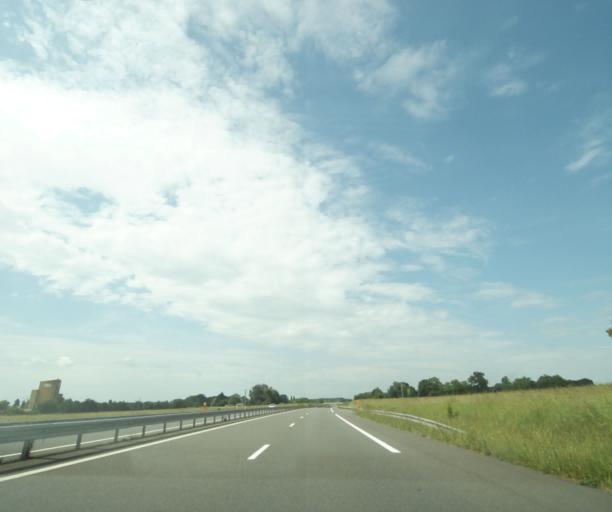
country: FR
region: Pays de la Loire
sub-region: Departement de Maine-et-Loire
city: Vivy
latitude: 47.3639
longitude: -0.0828
